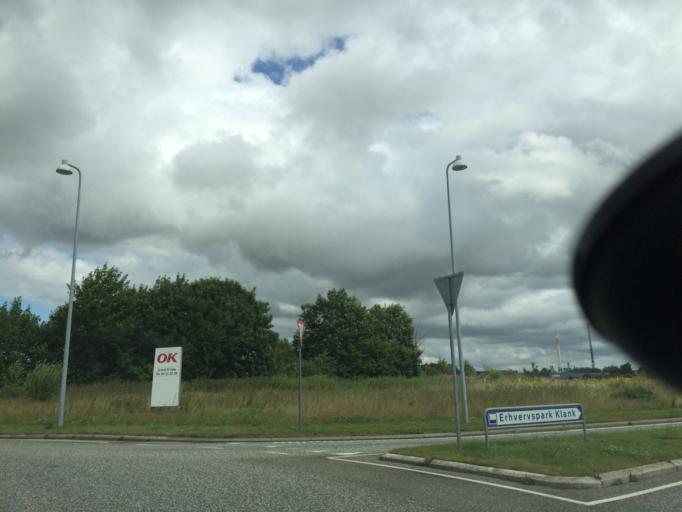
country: DK
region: Central Jutland
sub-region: Skanderborg Kommune
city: Galten
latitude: 56.1469
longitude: 9.9181
